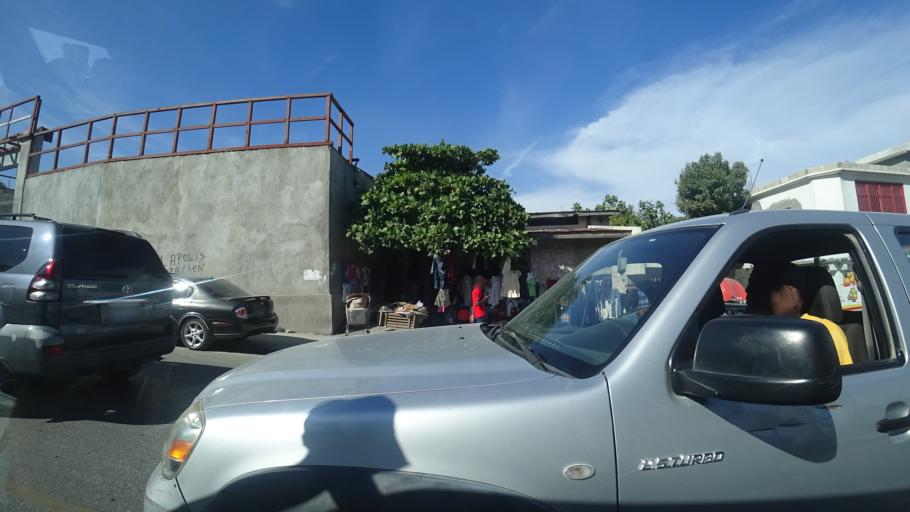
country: HT
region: Ouest
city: Delmas 73
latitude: 18.5520
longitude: -72.3164
